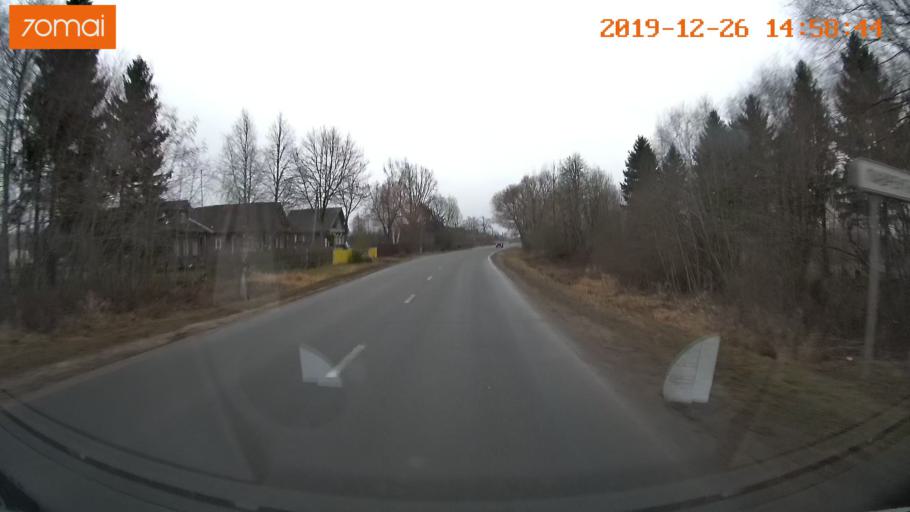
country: RU
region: Jaroslavl
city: Rybinsk
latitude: 58.2662
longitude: 38.8532
